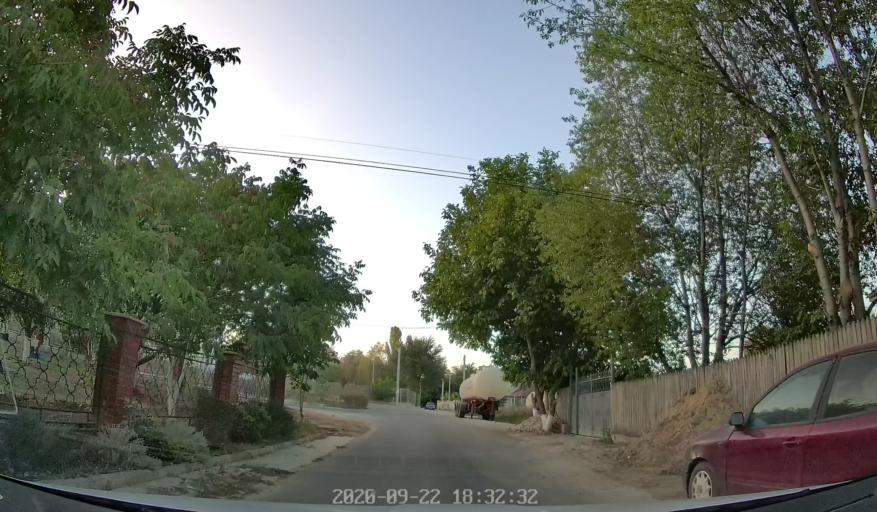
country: MD
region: Laloveni
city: Ialoveni
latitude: 46.9621
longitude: 28.7573
